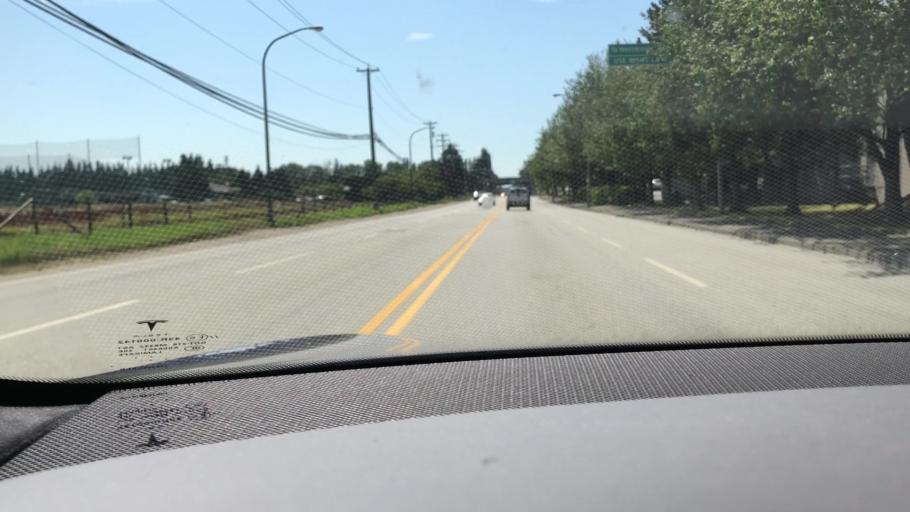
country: CA
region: British Columbia
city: Richmond
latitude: 49.1814
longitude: -123.0691
